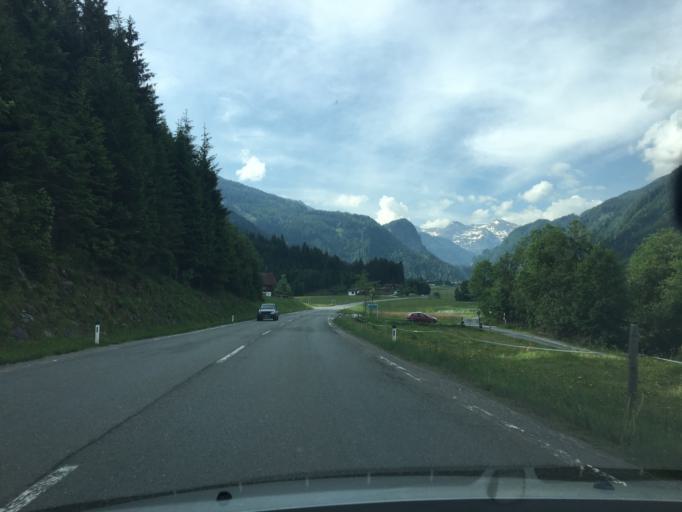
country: AT
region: Salzburg
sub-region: Politischer Bezirk Sankt Johann im Pongau
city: Untertauern
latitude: 47.3246
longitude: 13.5086
